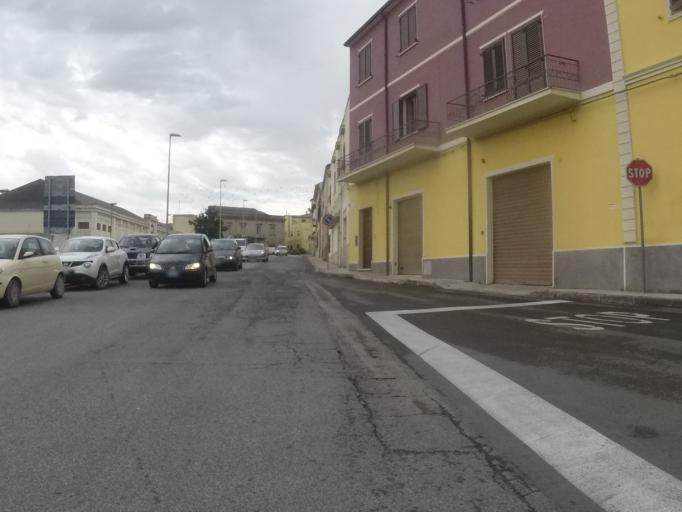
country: IT
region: Sardinia
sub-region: Provincia di Sassari
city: Sorso
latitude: 40.8009
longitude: 8.5808
